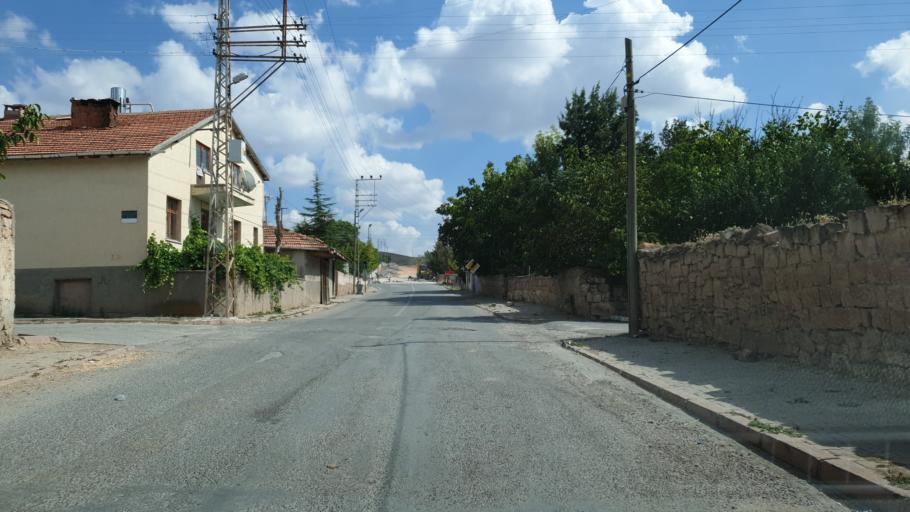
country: TR
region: Kayseri
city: Felahiye
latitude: 39.0893
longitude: 35.5637
